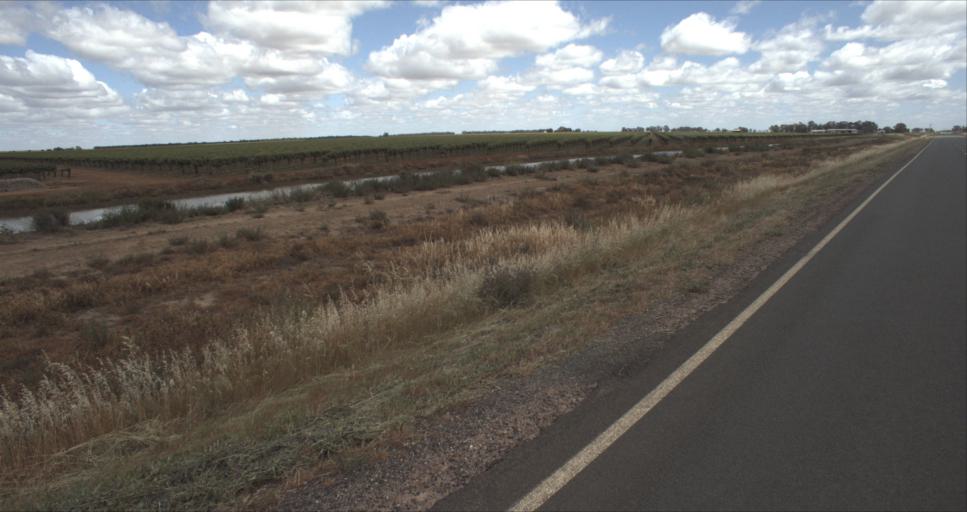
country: AU
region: New South Wales
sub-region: Murrumbidgee Shire
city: Darlington Point
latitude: -34.4922
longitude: 146.1661
